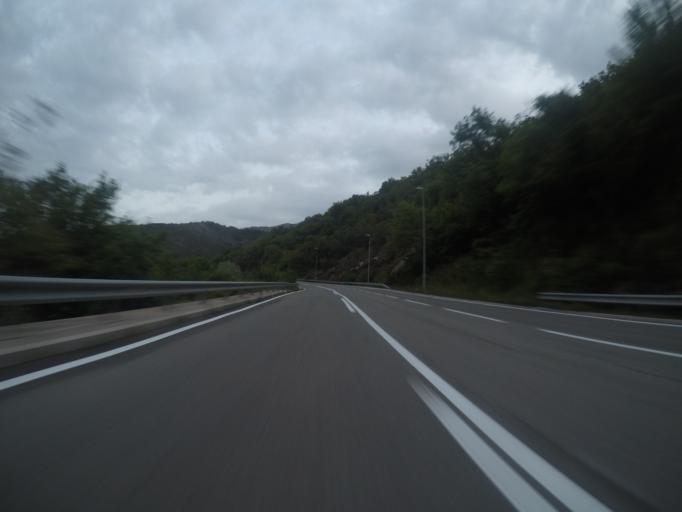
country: ME
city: Petrovac na Moru
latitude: 42.2074
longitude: 18.9492
